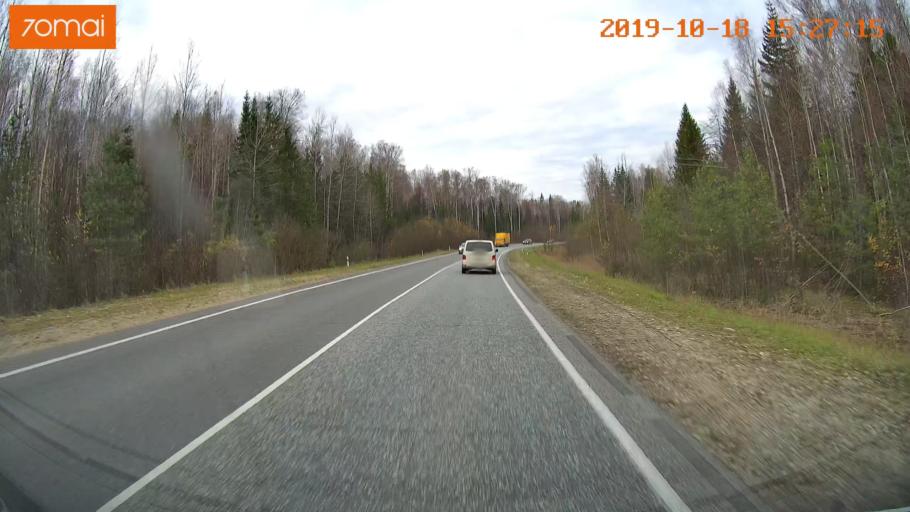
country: RU
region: Vladimir
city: Anopino
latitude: 55.7509
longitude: 40.6715
